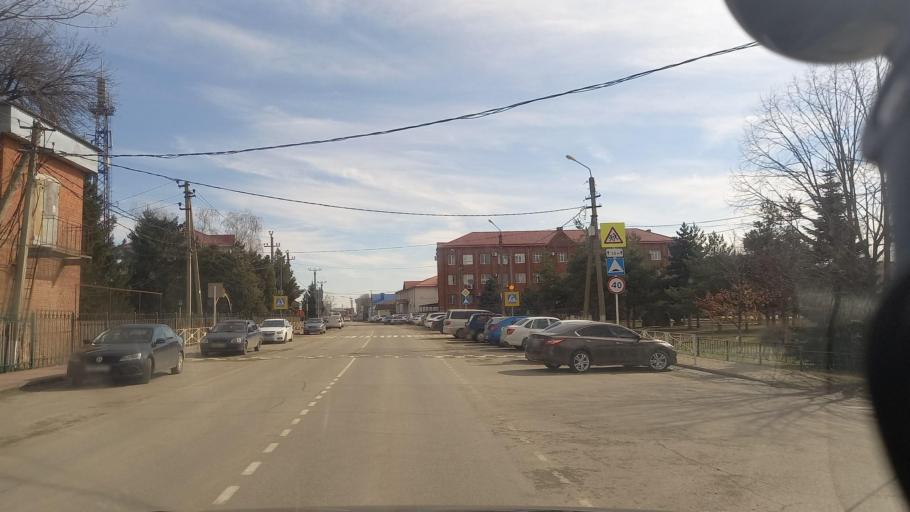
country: RU
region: Adygeya
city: Takhtamukay
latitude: 44.9259
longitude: 38.9898
